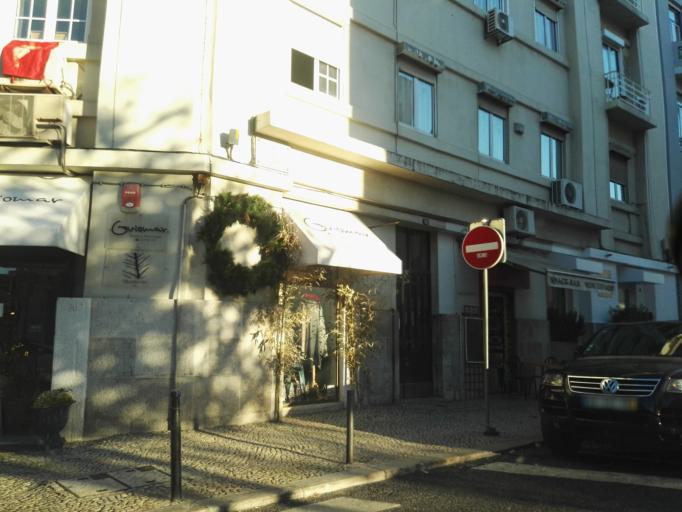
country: PT
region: Lisbon
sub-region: Lisbon
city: Lisbon
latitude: 38.7236
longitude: -9.1546
